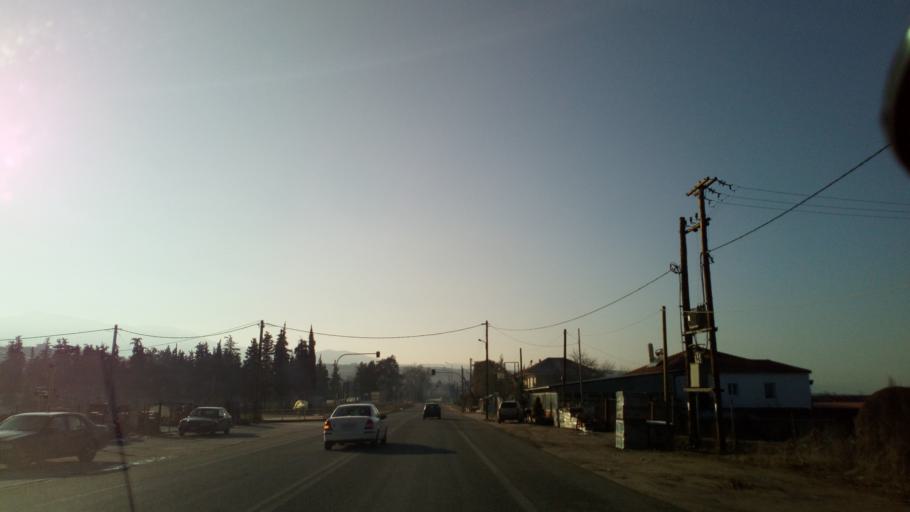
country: GR
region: Central Macedonia
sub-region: Nomos Thessalonikis
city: Gerakarou
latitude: 40.6310
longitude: 23.2158
